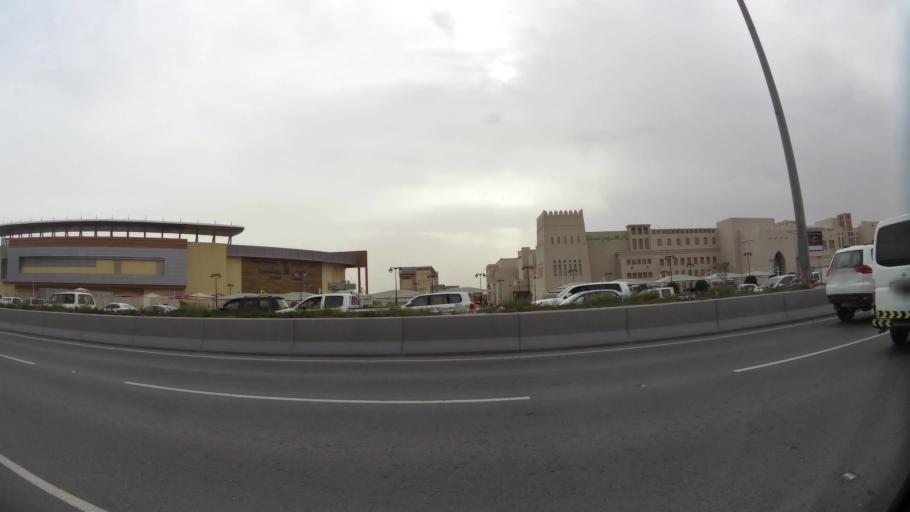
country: QA
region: Baladiyat ar Rayyan
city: Ar Rayyan
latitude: 25.3352
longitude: 51.4629
